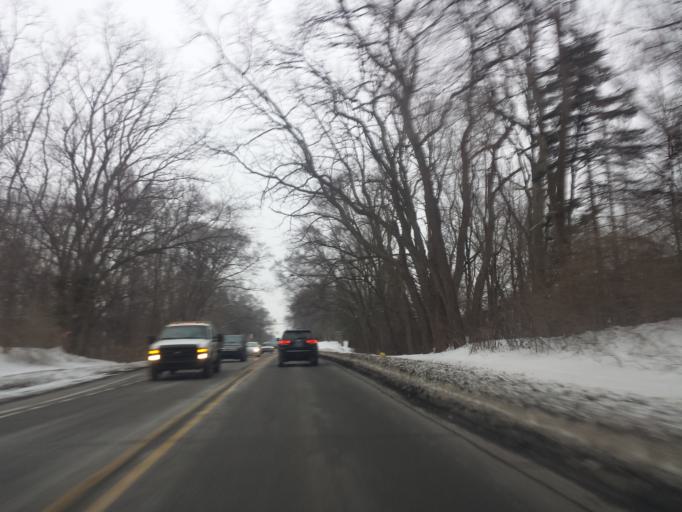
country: US
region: Michigan
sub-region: Oakland County
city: Franklin
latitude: 42.5102
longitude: -83.3397
